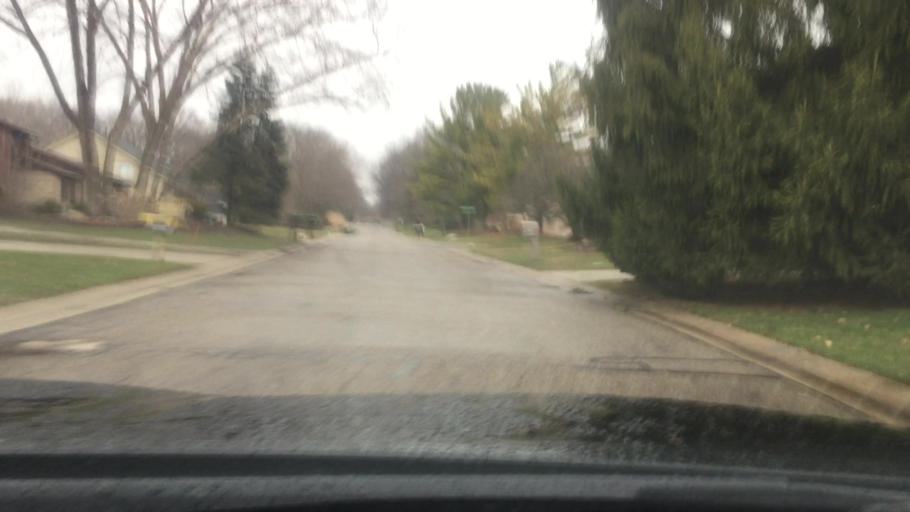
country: US
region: Michigan
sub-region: Oakland County
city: Farmington Hills
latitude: 42.5061
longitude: -83.4036
